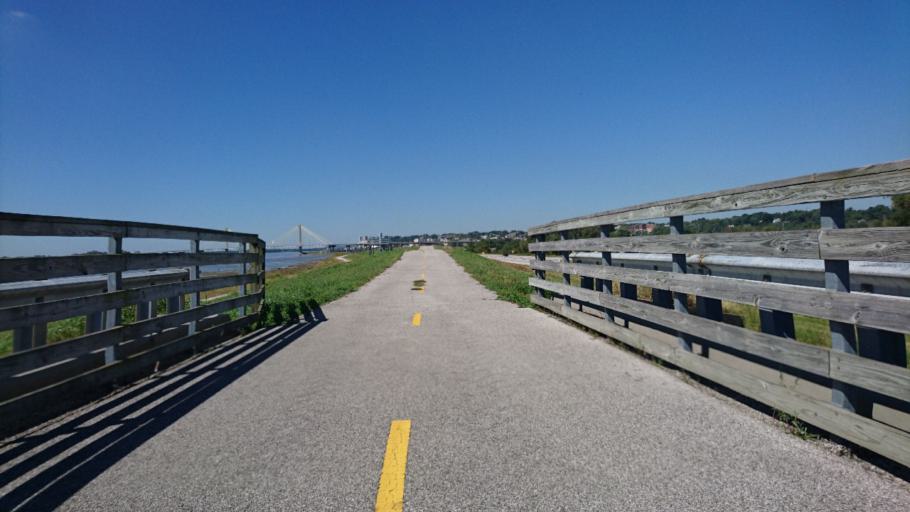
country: US
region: Illinois
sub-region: Madison County
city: Alton
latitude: 38.8780
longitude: -90.1600
